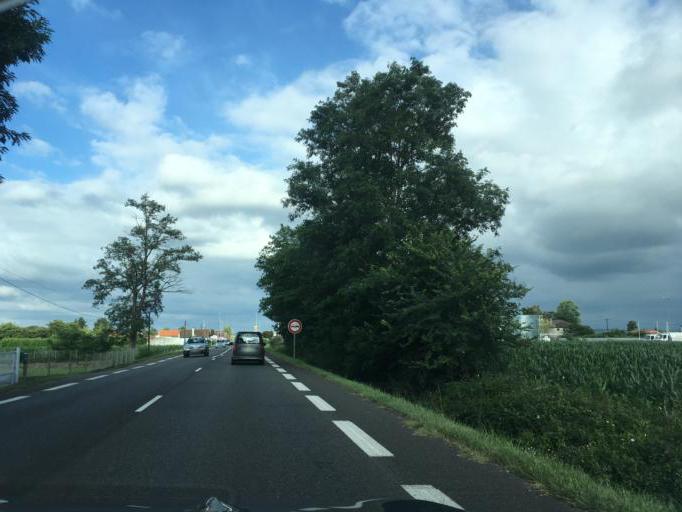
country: FR
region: Midi-Pyrenees
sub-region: Departement des Hautes-Pyrenees
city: Ibos
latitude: 43.2395
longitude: 0.0267
